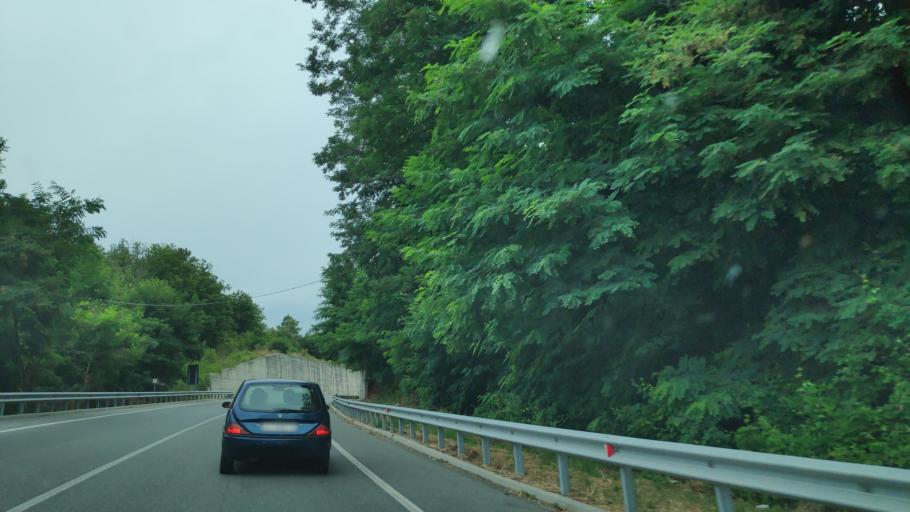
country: IT
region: Calabria
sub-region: Provincia di Catanzaro
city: Chiaravalle Centrale
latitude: 38.6684
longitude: 16.4026
